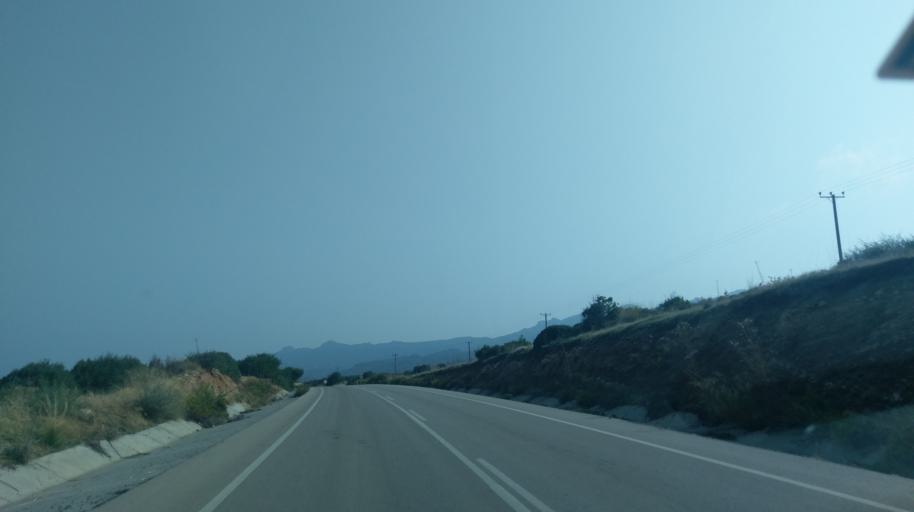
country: CY
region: Ammochostos
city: Trikomo
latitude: 35.4098
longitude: 33.8220
